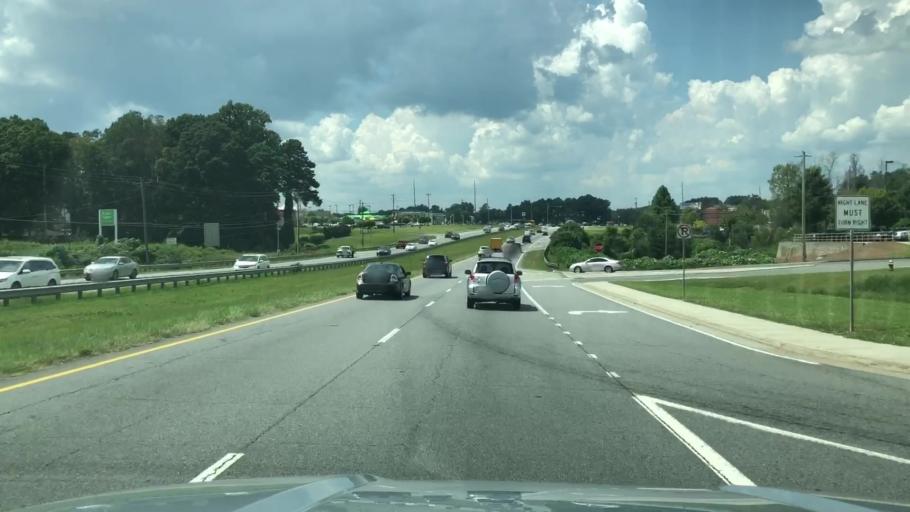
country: US
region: Georgia
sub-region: Cobb County
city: Acworth
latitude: 34.0371
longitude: -84.6874
